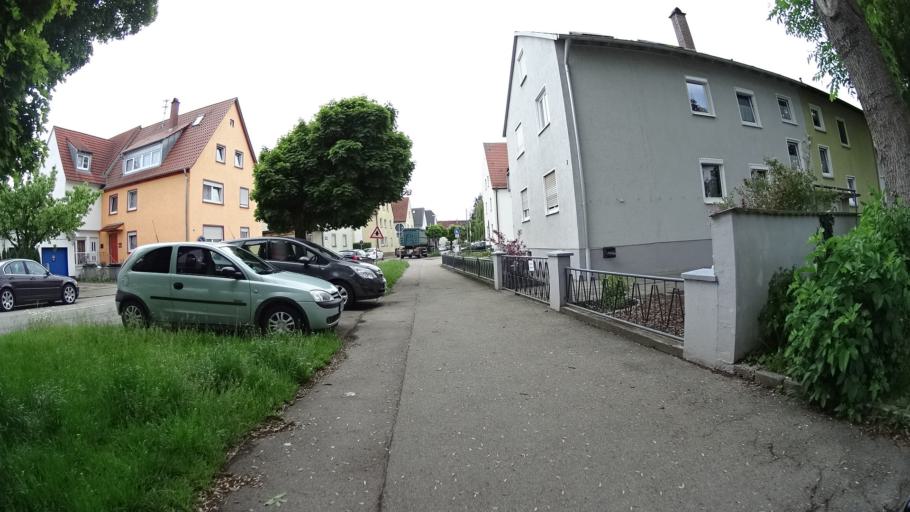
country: DE
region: Bavaria
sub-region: Swabia
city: Weissenhorn
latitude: 48.3109
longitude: 10.1576
